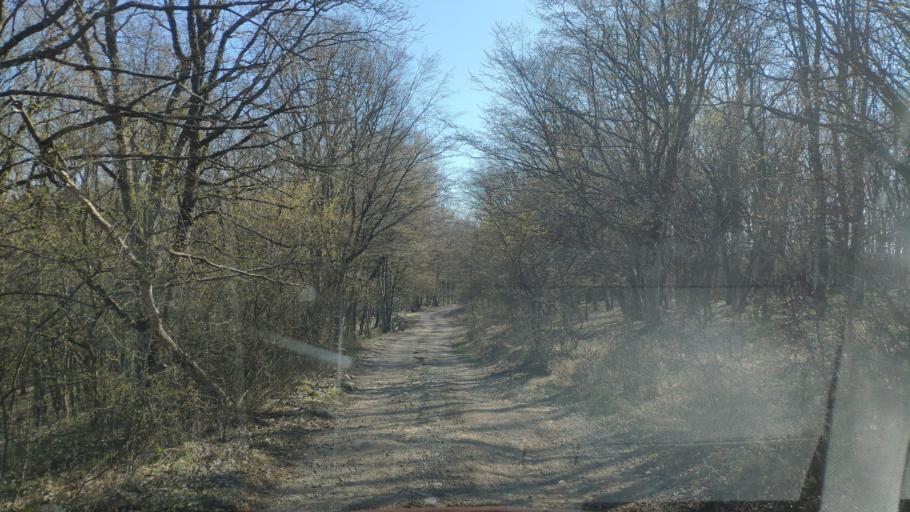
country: SK
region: Kosicky
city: Roznava
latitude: 48.6058
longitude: 20.4150
